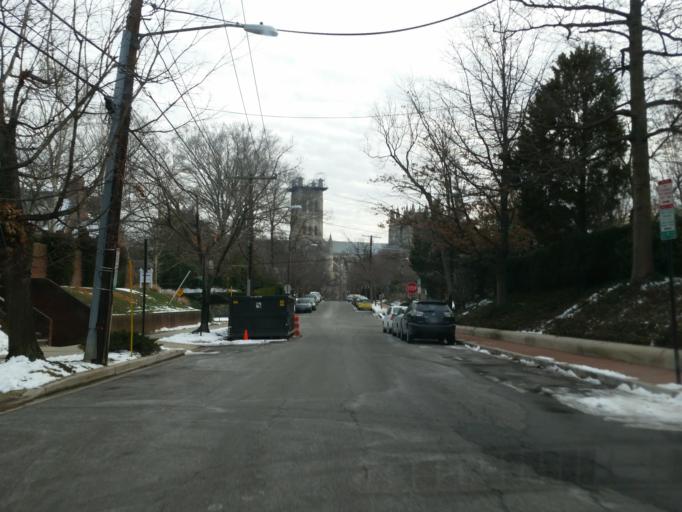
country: US
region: Maryland
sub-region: Montgomery County
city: Friendship Village
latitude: 38.9352
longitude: -77.0709
